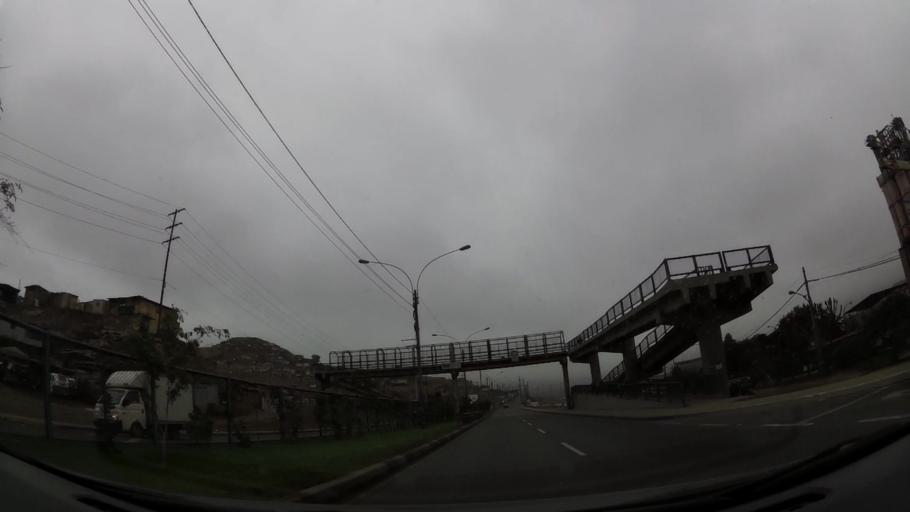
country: PE
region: Lima
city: Ventanilla
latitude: -11.8673
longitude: -77.1282
